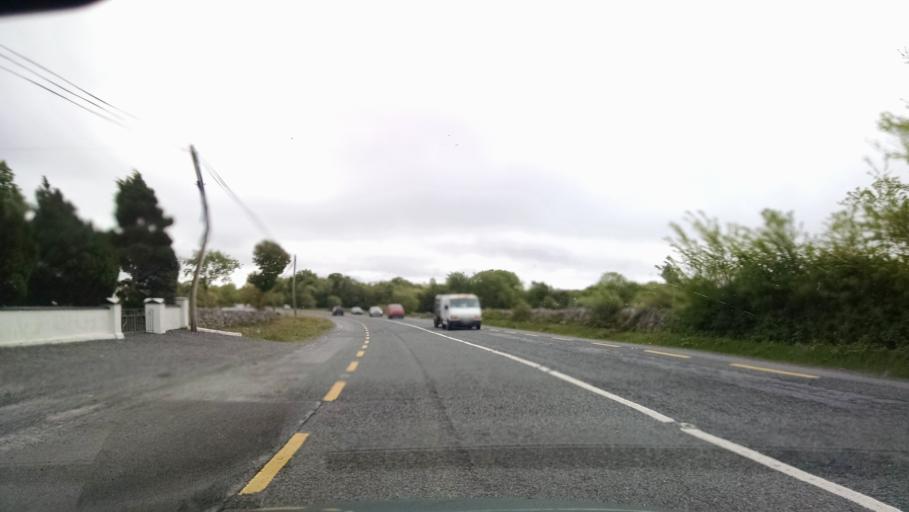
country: IE
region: Connaught
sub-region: County Galway
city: Claregalway
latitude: 53.4212
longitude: -9.0327
